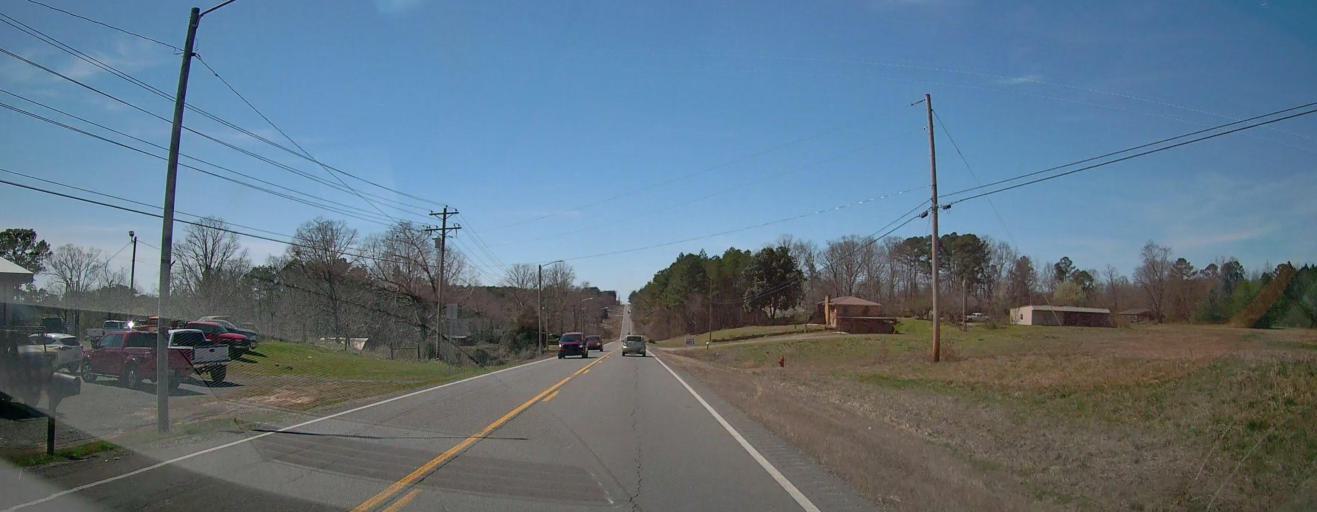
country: US
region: Alabama
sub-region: Blount County
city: Blountsville
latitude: 34.1745
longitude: -86.6236
